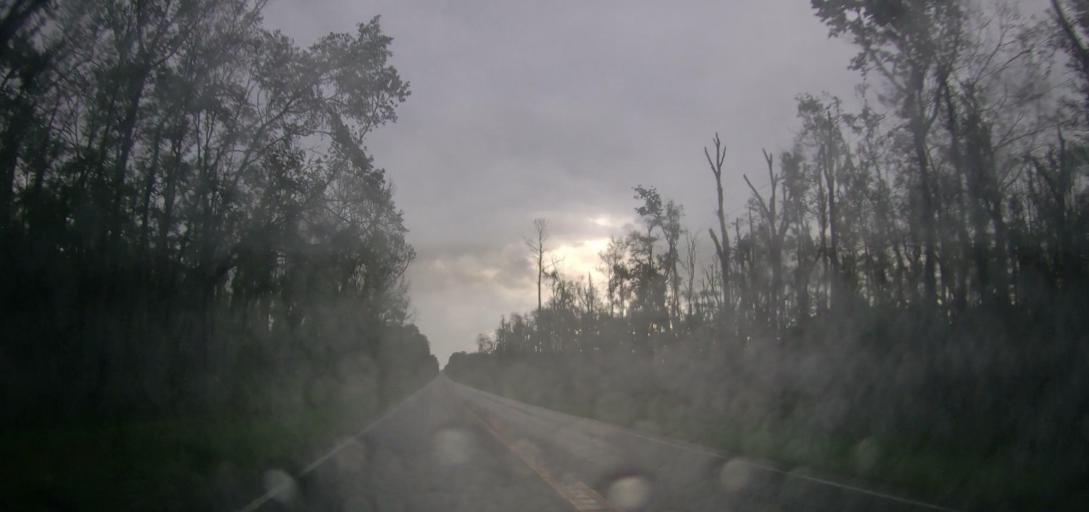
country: US
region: Georgia
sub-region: Brantley County
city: Nahunta
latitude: 31.3206
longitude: -81.7530
